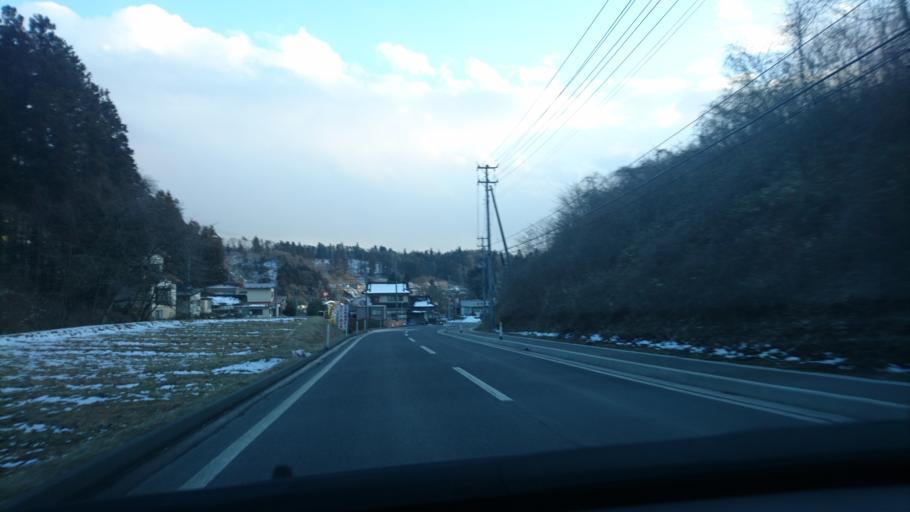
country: JP
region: Iwate
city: Ichinoseki
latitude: 39.0009
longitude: 141.3333
